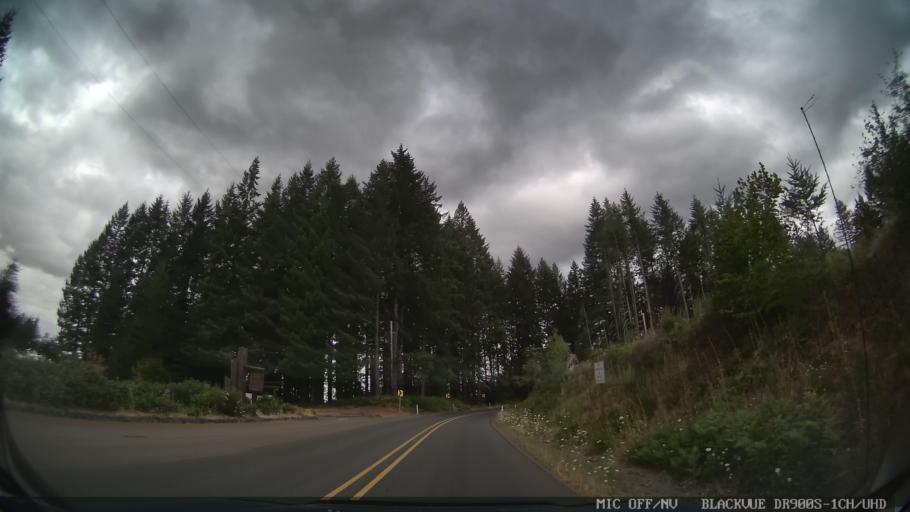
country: US
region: Oregon
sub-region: Linn County
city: Lyons
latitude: 44.8522
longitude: -122.6639
